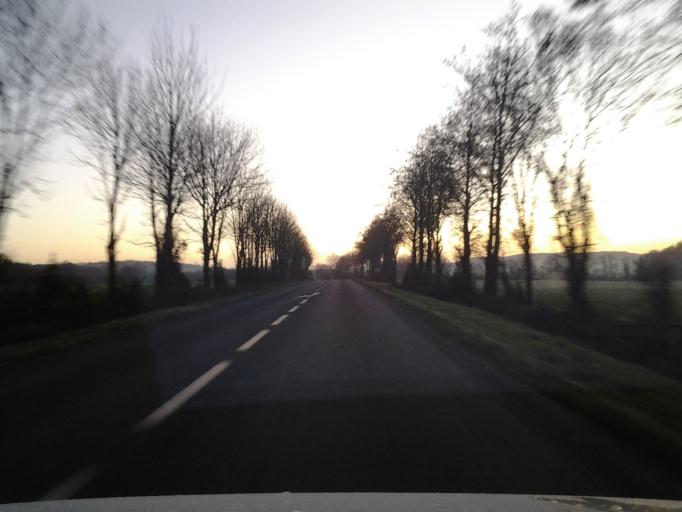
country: FR
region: Pays de la Loire
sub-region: Departement de la Vendee
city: Les Herbiers
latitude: 46.8700
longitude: -0.9708
